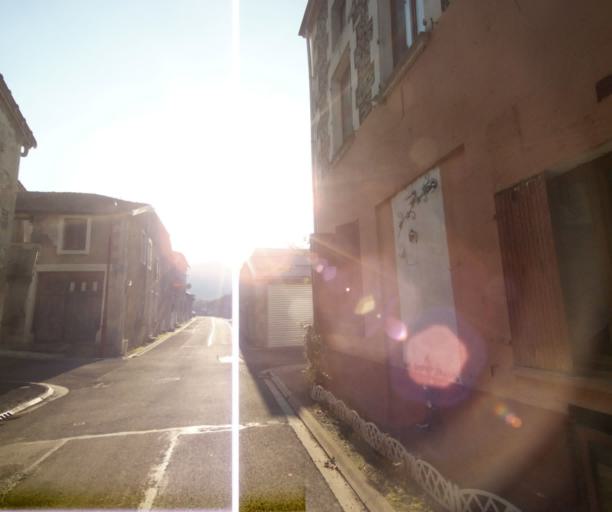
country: FR
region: Champagne-Ardenne
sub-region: Departement de la Haute-Marne
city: Chevillon
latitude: 48.4953
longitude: 5.1916
